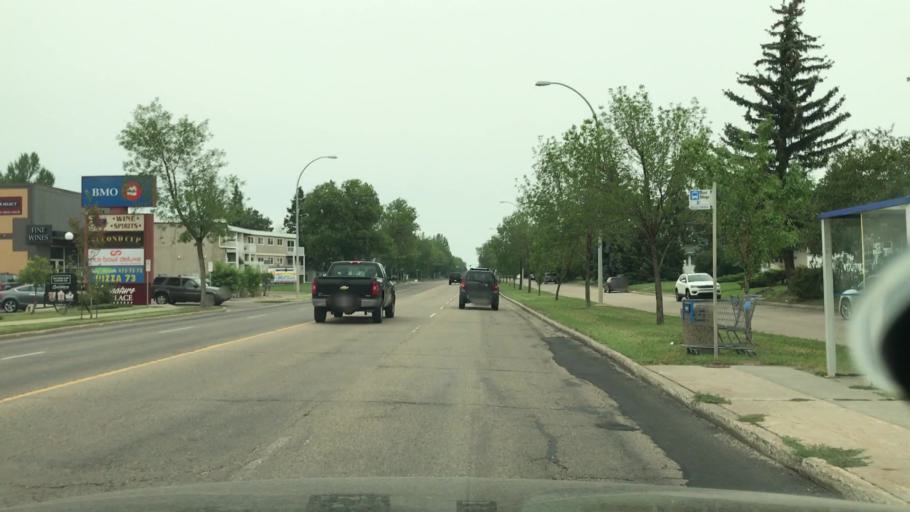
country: CA
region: Alberta
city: Edmonton
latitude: 53.5214
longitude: -113.5779
